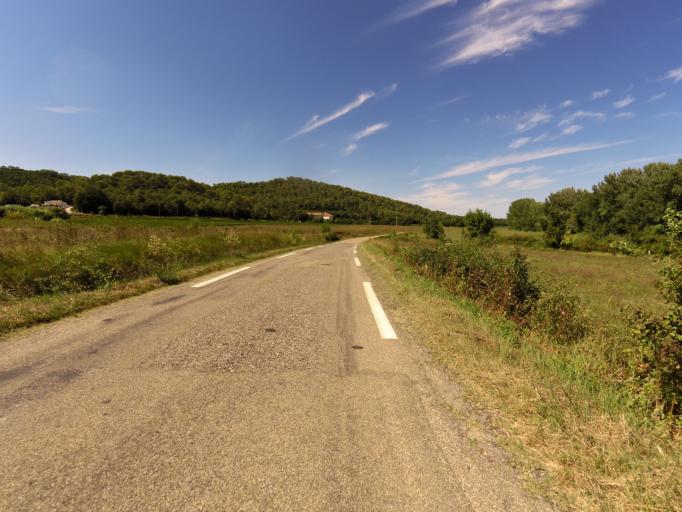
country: FR
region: Languedoc-Roussillon
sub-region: Departement du Gard
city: Quissac
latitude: 43.8586
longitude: 4.0424
